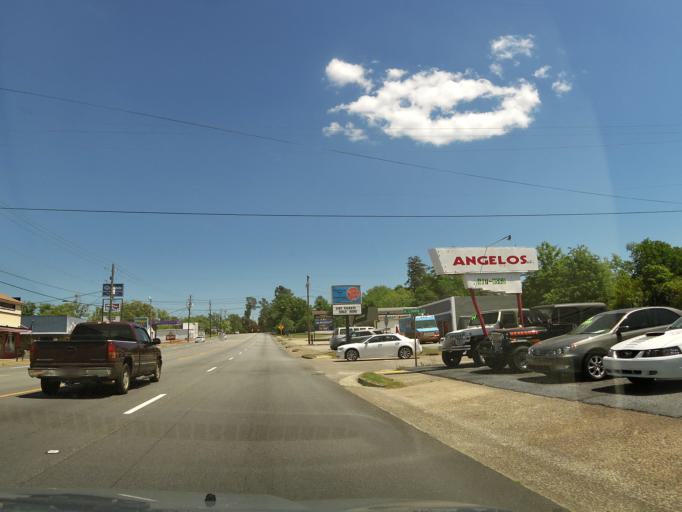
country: US
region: South Carolina
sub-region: Aiken County
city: Aiken
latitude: 33.5655
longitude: -81.7341
